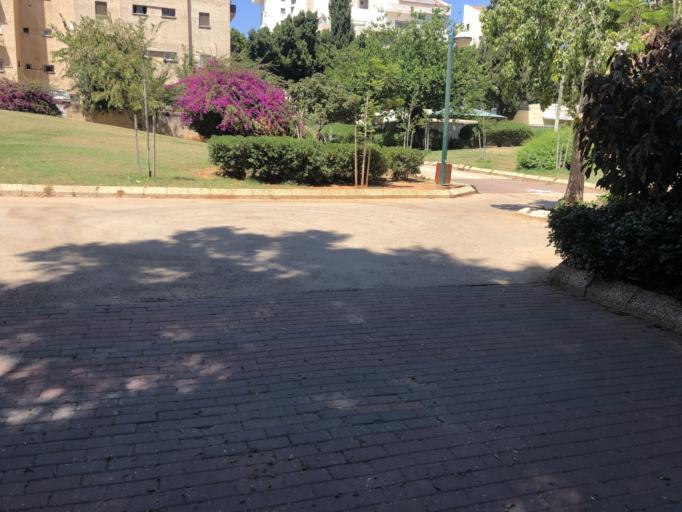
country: IL
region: Central District
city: Kfar Saba
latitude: 32.1764
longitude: 34.9131
